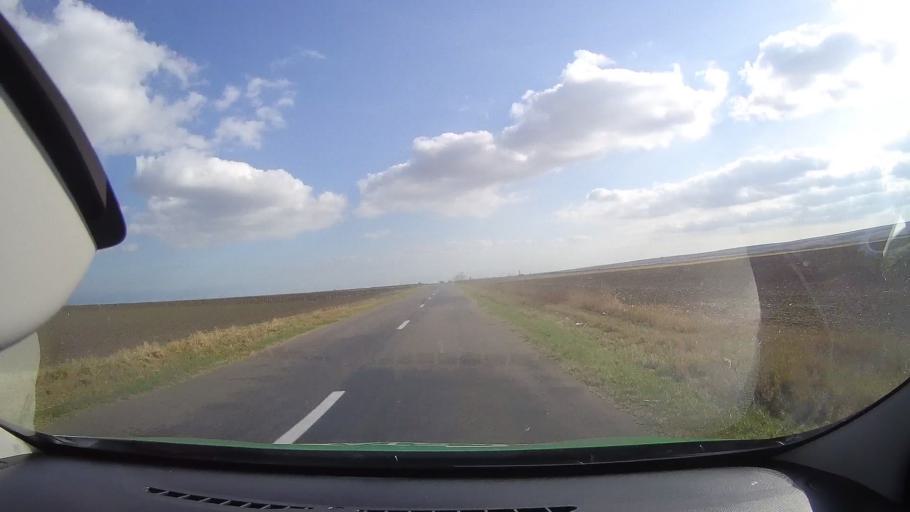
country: RO
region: Constanta
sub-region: Comuna Cogealac
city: Tariverde
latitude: 44.5579
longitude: 28.6134
